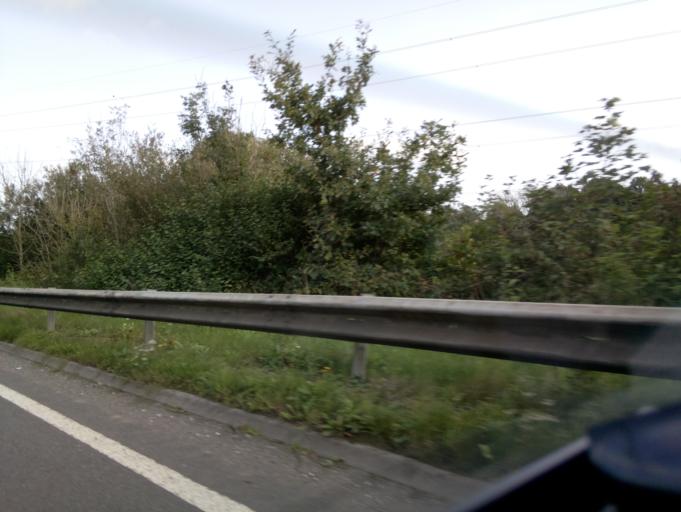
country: GB
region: Wales
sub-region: Rhondda Cynon Taf
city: Llantrisant
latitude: 51.5332
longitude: -3.3689
